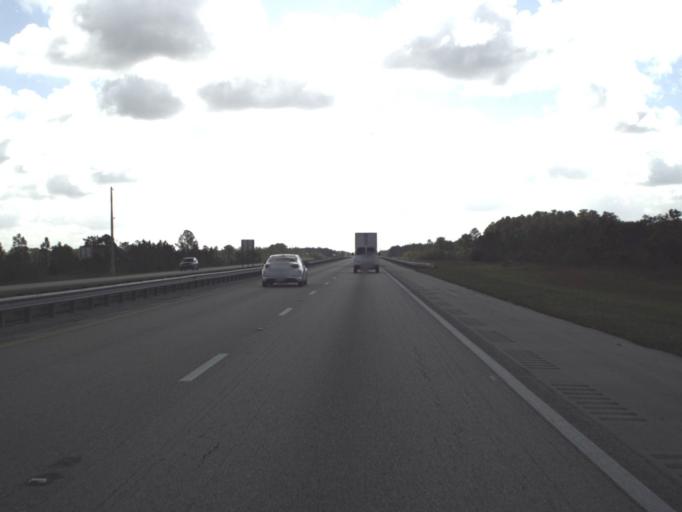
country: US
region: Florida
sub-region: Osceola County
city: Saint Cloud
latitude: 27.9963
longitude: -81.1342
